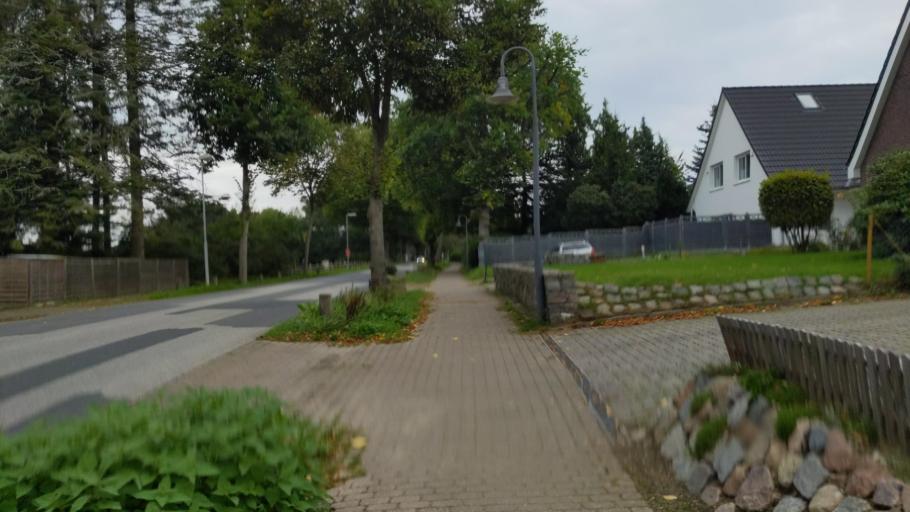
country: DE
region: Schleswig-Holstein
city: Krummesse
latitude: 53.7882
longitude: 10.6403
